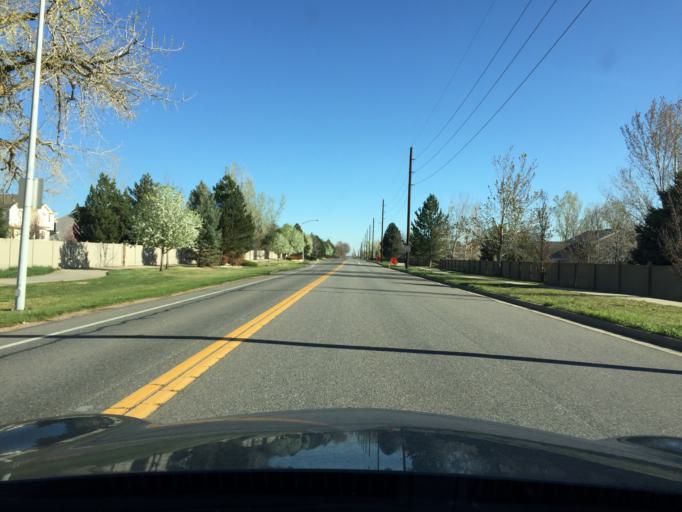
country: US
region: Colorado
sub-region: Boulder County
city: Erie
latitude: 40.0399
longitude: -105.0745
